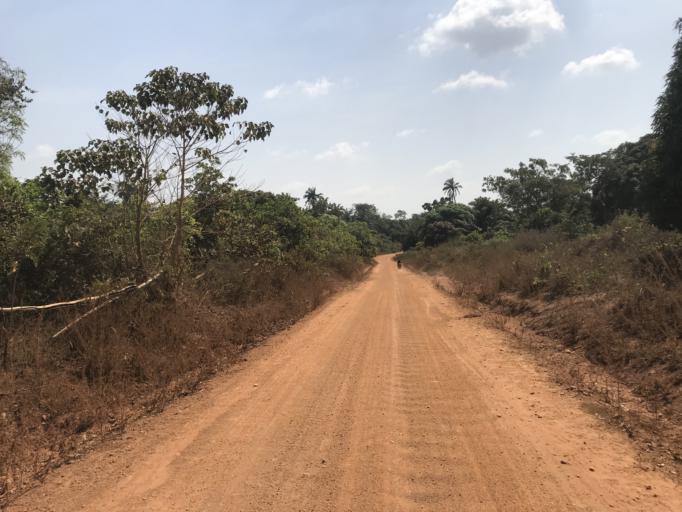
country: NG
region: Osun
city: Ifon
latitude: 7.9203
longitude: 4.4828
